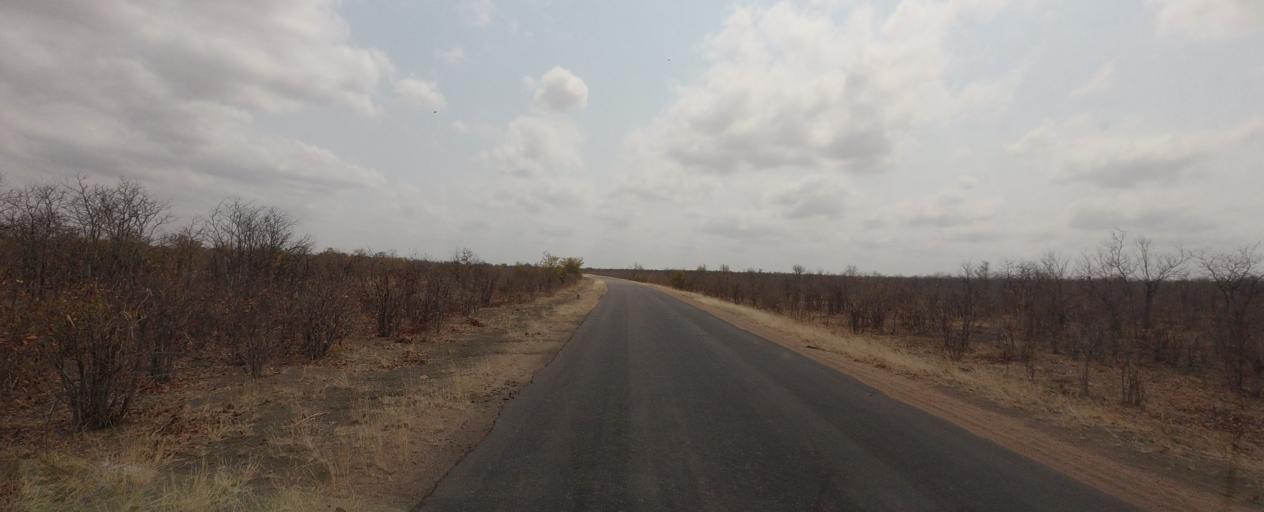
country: ZA
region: Limpopo
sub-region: Mopani District Municipality
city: Phalaborwa
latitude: -23.6003
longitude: 31.4551
